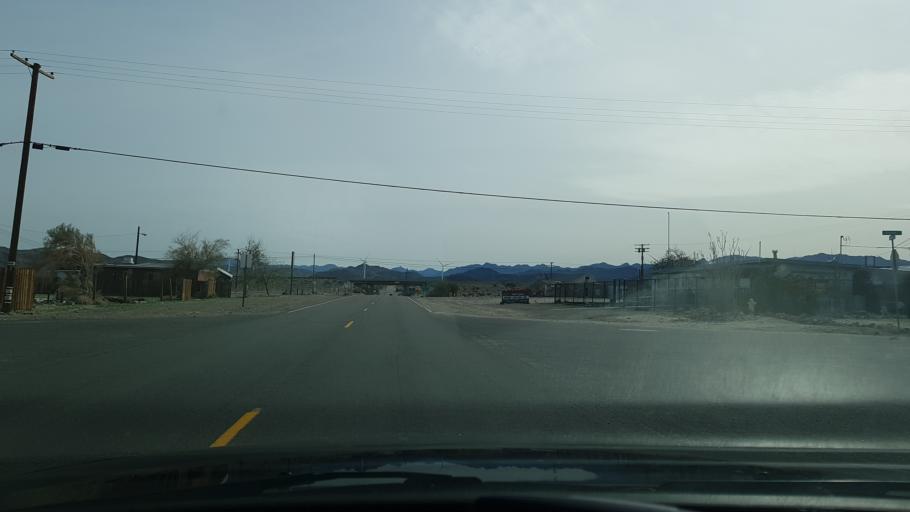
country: US
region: California
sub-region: Imperial County
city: Seeley
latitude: 32.7370
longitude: -115.9943
